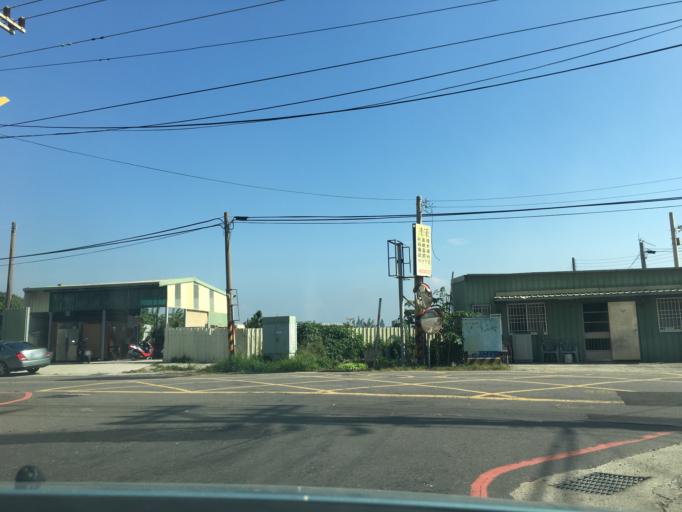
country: TW
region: Taiwan
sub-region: Hsinchu
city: Hsinchu
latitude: 24.8080
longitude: 120.9219
